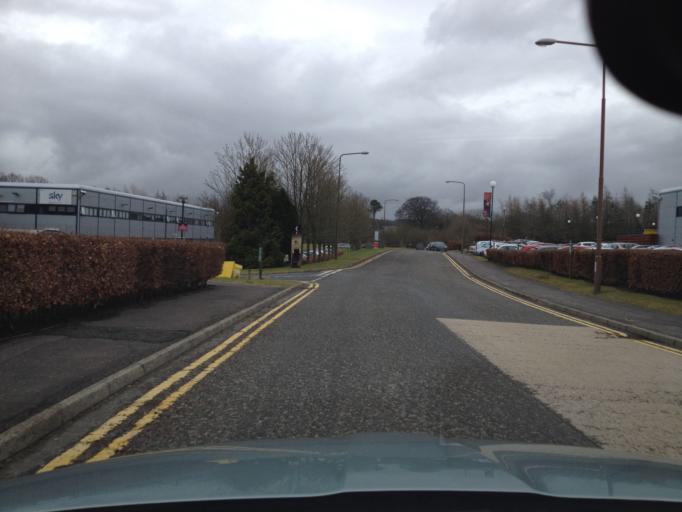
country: GB
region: Scotland
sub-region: West Lothian
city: West Calder
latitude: 55.8773
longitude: -3.5534
